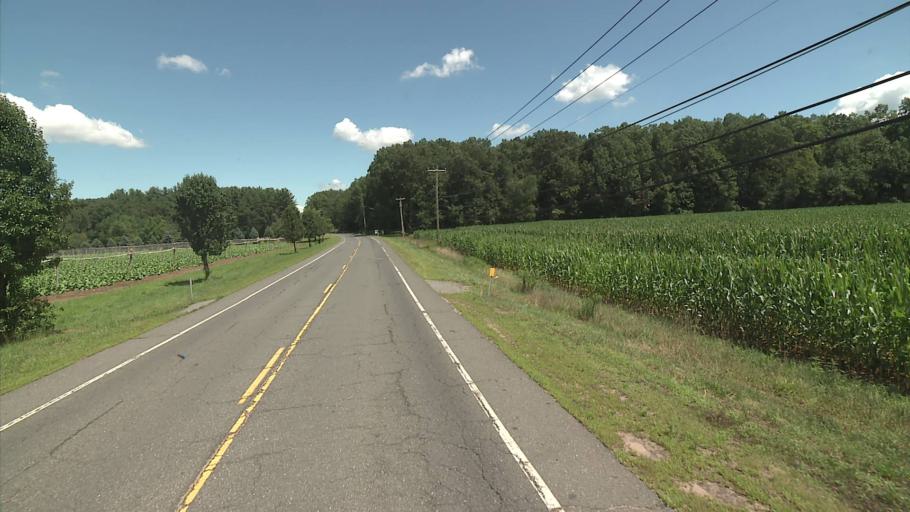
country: US
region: Massachusetts
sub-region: Hampden County
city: Southwick
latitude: 42.0193
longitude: -72.7403
